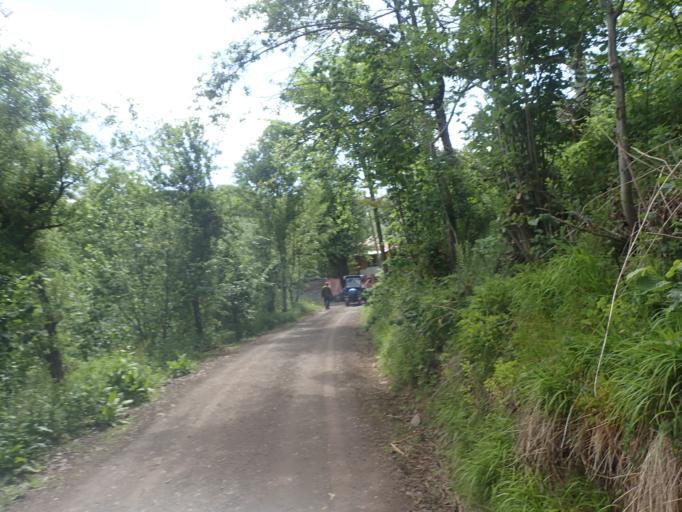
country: TR
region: Ordu
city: Akkus
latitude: 40.9060
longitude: 36.8834
